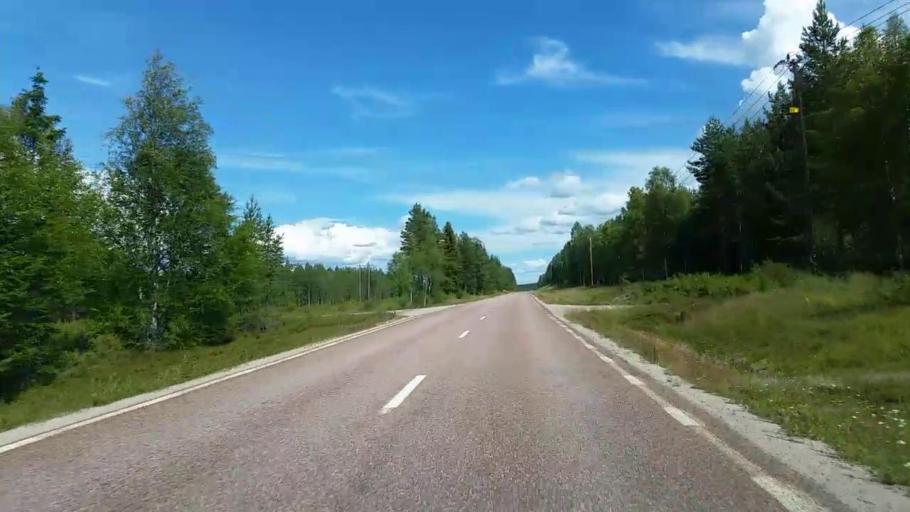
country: SE
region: Dalarna
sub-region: Rattviks Kommun
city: Raettvik
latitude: 61.1902
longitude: 15.3161
